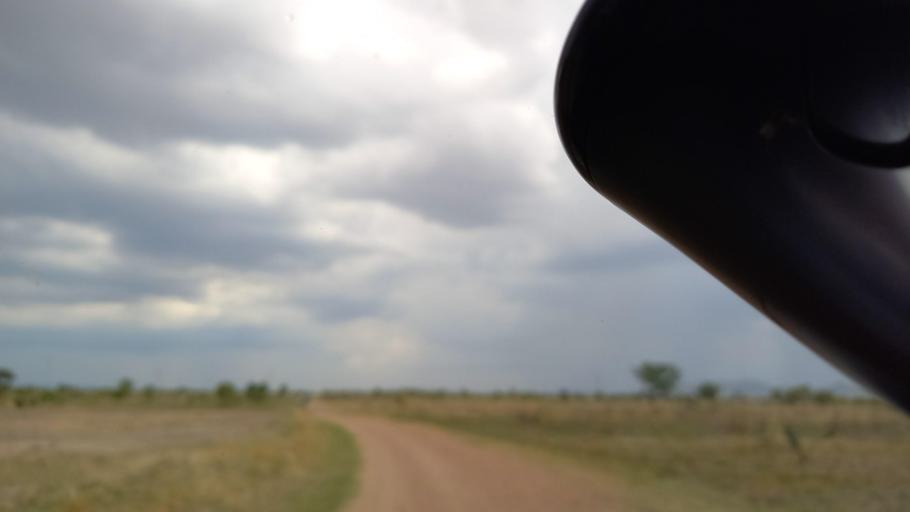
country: ZM
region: Lusaka
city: Kafue
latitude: -15.8446
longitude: 28.0956
